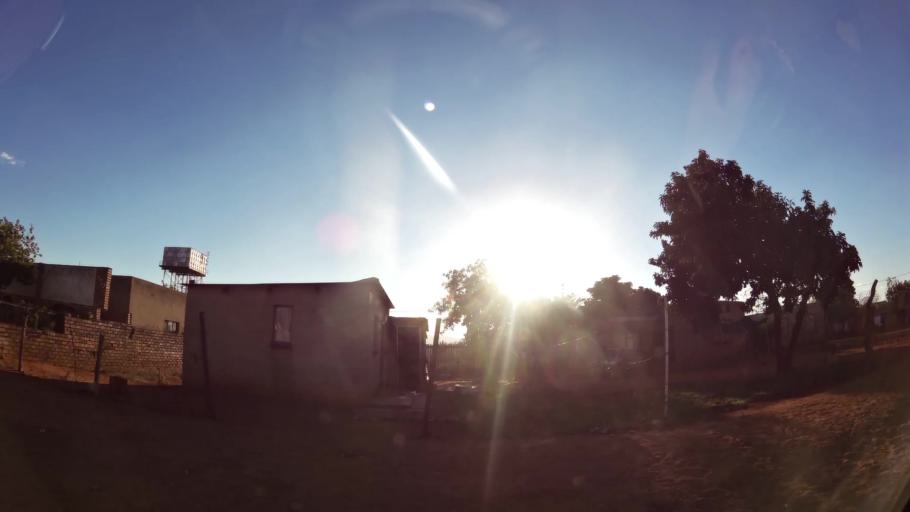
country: ZA
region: Limpopo
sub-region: Waterberg District Municipality
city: Mokopane
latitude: -24.1518
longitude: 28.9917
